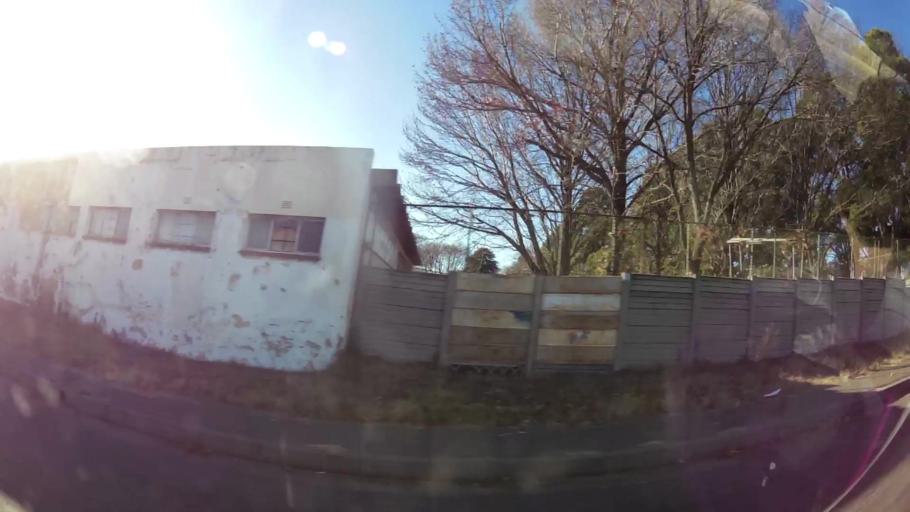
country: ZA
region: Gauteng
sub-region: West Rand District Municipality
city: Krugersdorp
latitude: -26.1019
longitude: 27.7797
